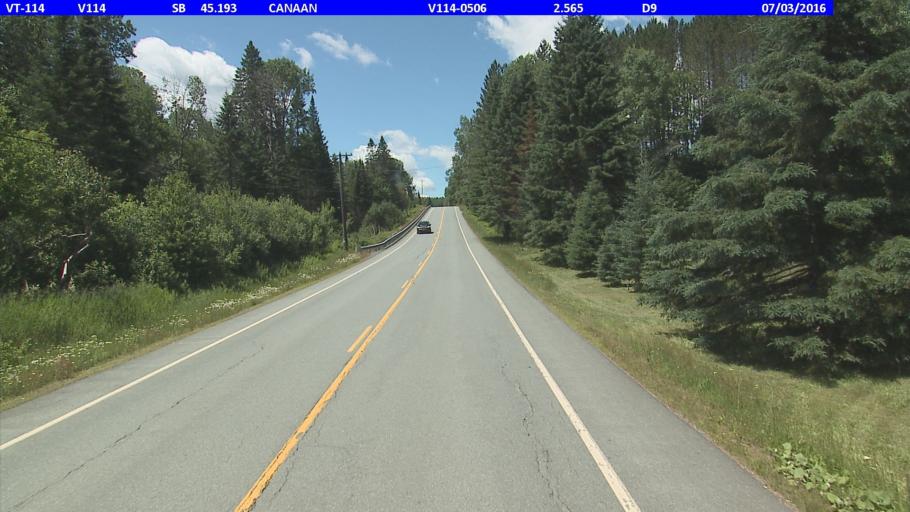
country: US
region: New Hampshire
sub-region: Coos County
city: Colebrook
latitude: 45.0063
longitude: -71.6418
